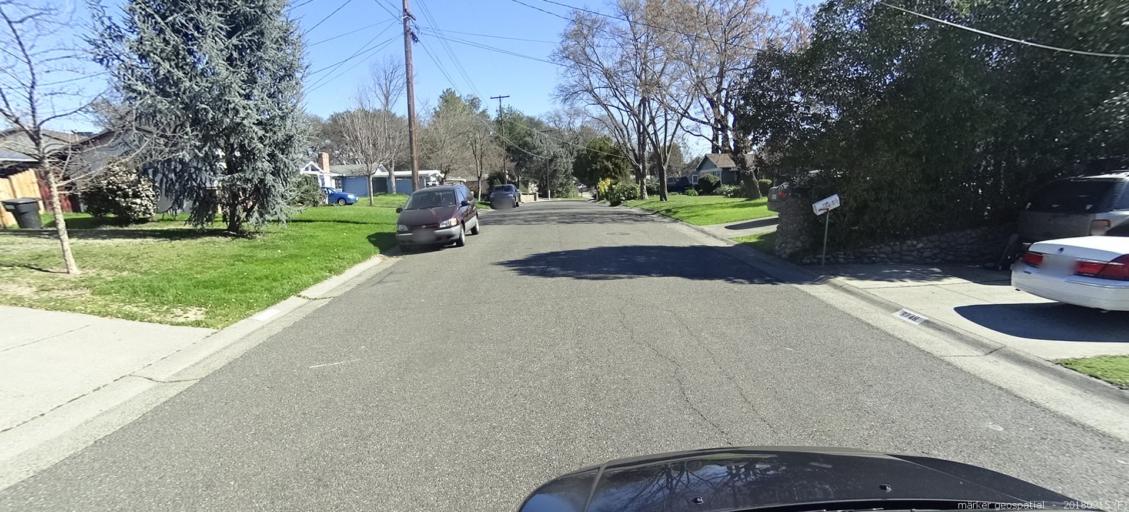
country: US
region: California
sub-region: Sacramento County
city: Fair Oaks
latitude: 38.6704
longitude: -121.3062
